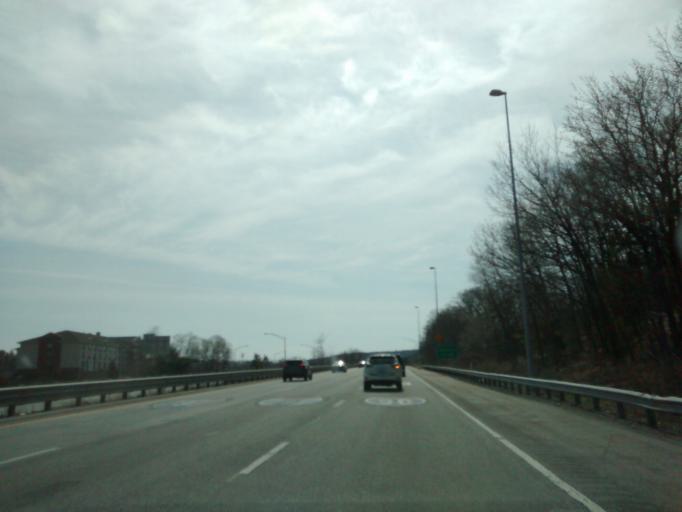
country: US
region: Massachusetts
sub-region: Worcester County
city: Auburn
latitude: 42.1946
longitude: -71.8460
